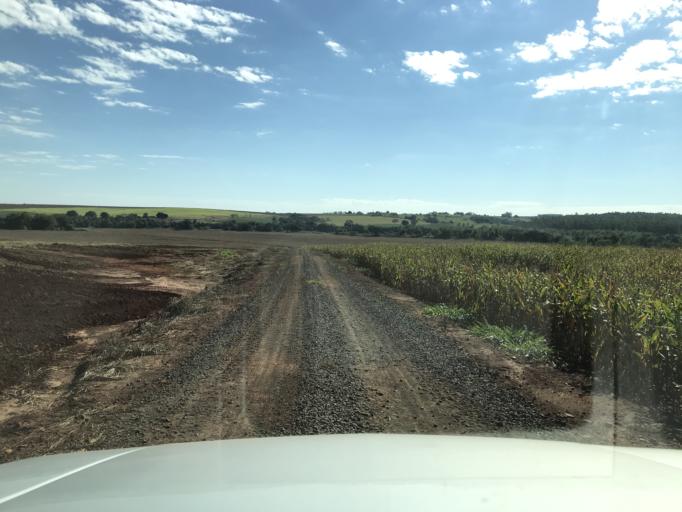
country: BR
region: Parana
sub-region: Palotina
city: Palotina
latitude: -24.1579
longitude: -53.7430
